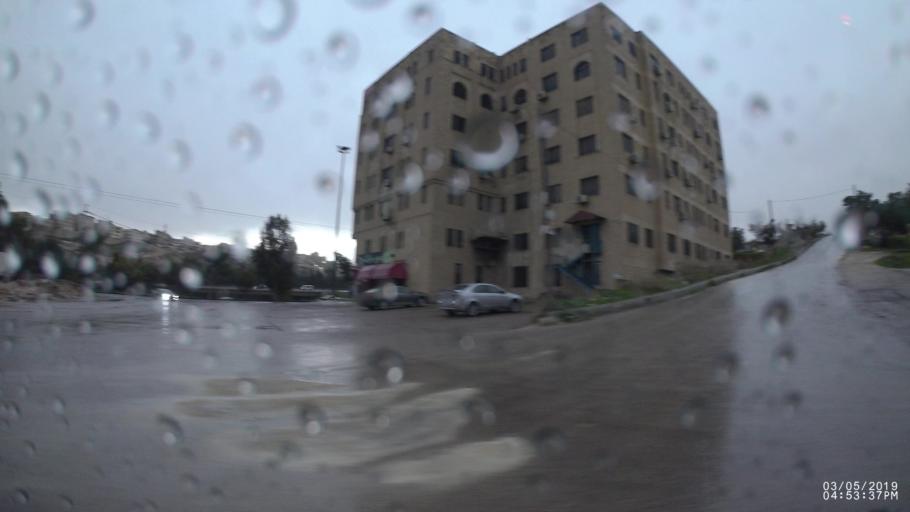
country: JO
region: Amman
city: Amman
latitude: 31.9909
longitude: 35.9772
